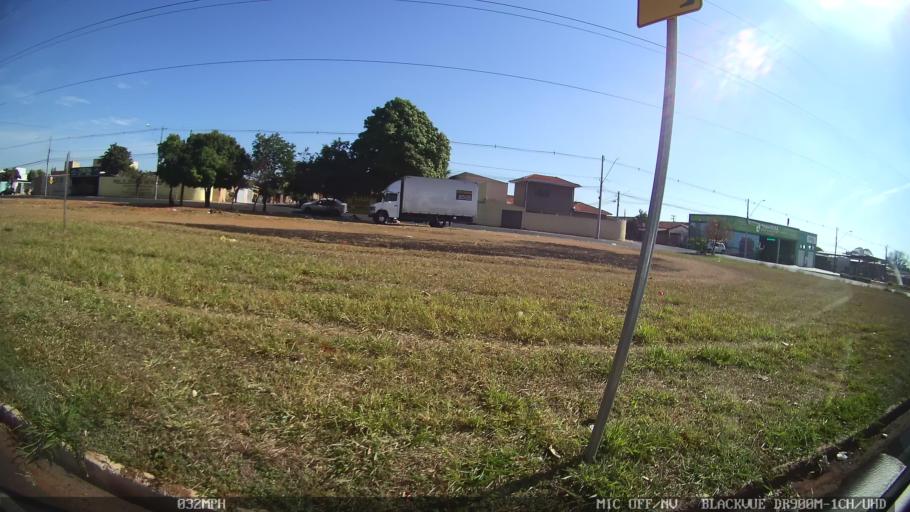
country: BR
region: Sao Paulo
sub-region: Sao Jose Do Rio Preto
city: Sao Jose do Rio Preto
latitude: -20.7801
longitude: -49.4042
